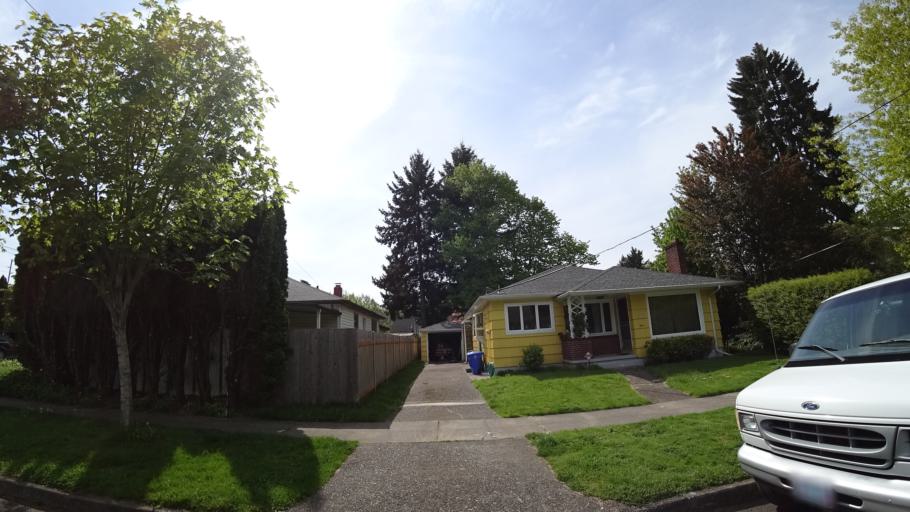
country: US
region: Oregon
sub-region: Clackamas County
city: Milwaukie
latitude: 45.4824
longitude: -122.6144
